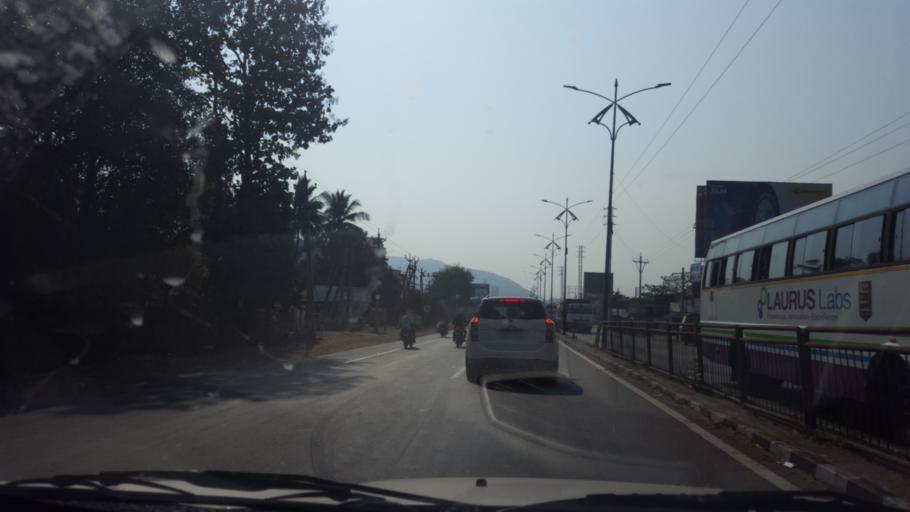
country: IN
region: Andhra Pradesh
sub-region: Vishakhapatnam
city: Anakapalle
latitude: 17.6885
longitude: 83.0993
